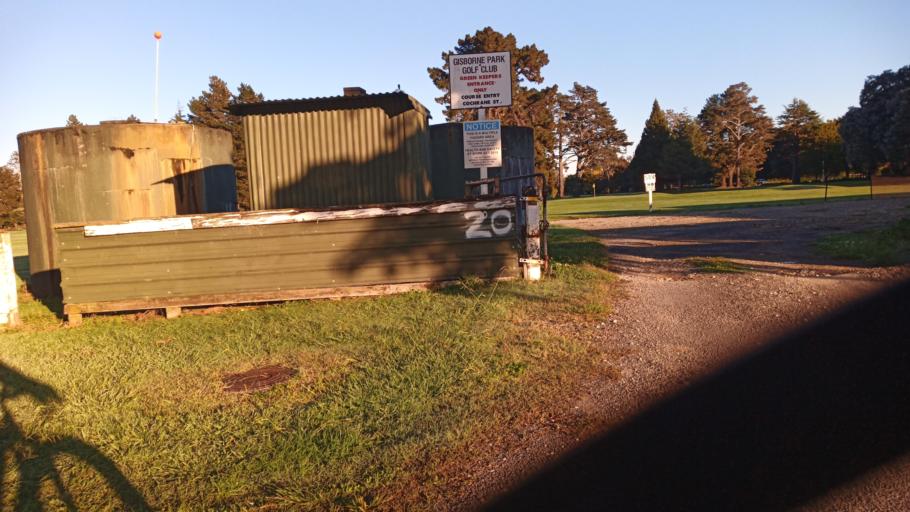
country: NZ
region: Gisborne
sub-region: Gisborne District
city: Gisborne
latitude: -38.6511
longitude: 177.9895
